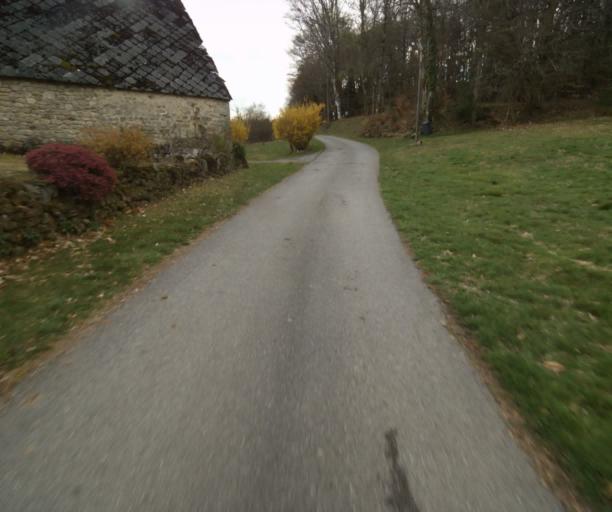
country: FR
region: Limousin
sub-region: Departement de la Correze
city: Argentat
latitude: 45.2268
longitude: 1.9478
